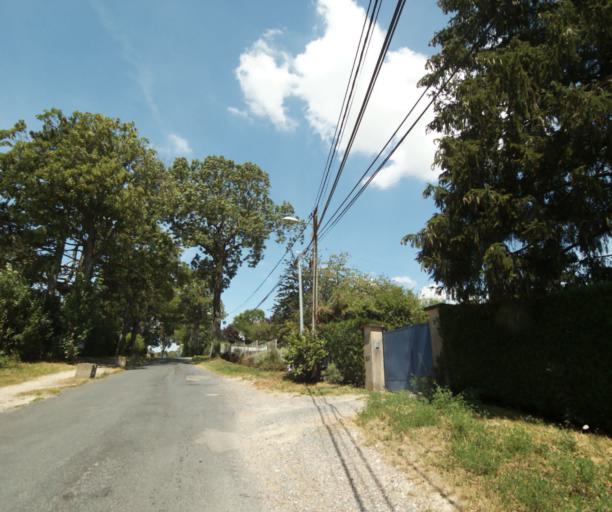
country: FR
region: Lorraine
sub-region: Departement de Meurthe-et-Moselle
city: Luneville
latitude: 48.6041
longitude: 6.4913
